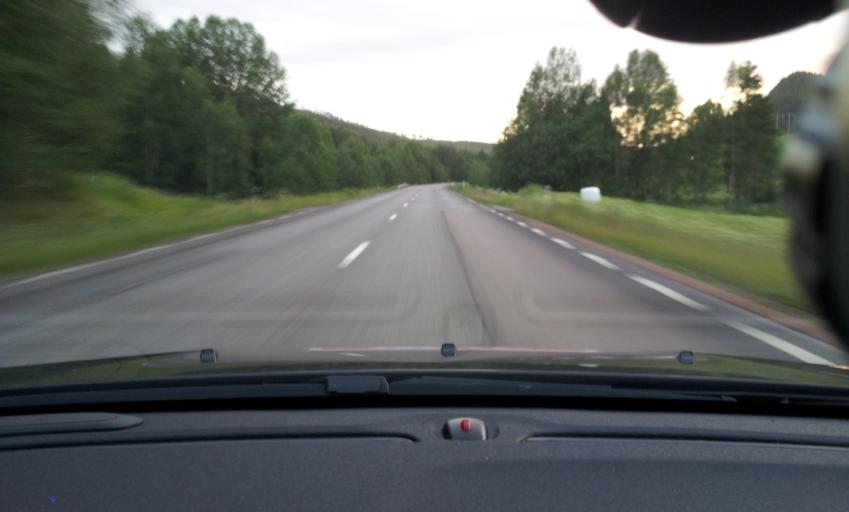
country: SE
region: Jaemtland
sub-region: Ragunda Kommun
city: Hammarstrand
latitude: 63.0924
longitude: 16.4424
